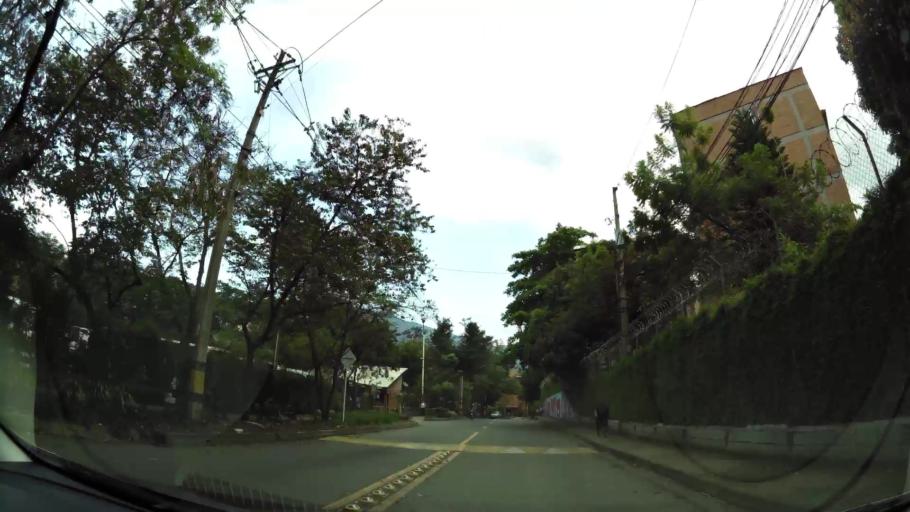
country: CO
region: Antioquia
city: Envigado
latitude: 6.1651
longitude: -75.5871
